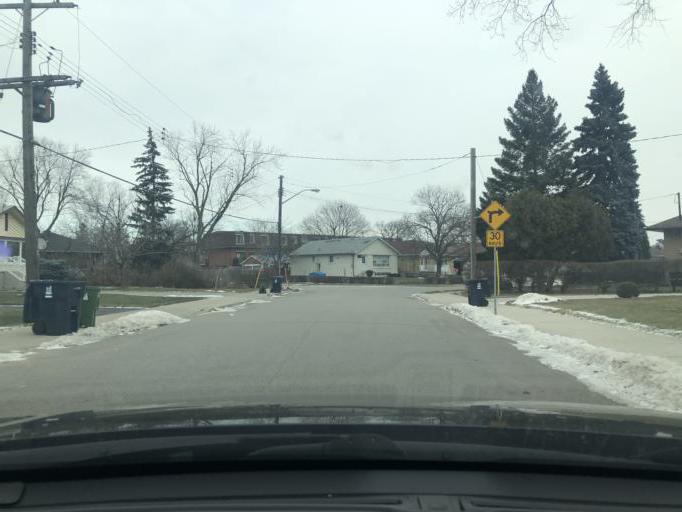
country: CA
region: Ontario
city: Scarborough
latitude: 43.7668
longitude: -79.3052
